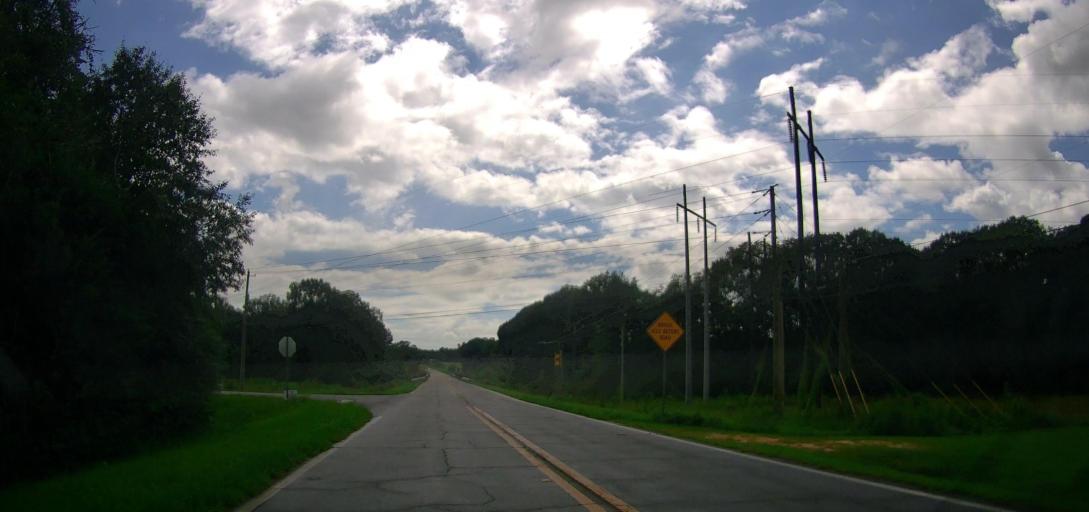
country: US
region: Georgia
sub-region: Ben Hill County
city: Fitzgerald
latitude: 31.7076
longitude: -83.2948
